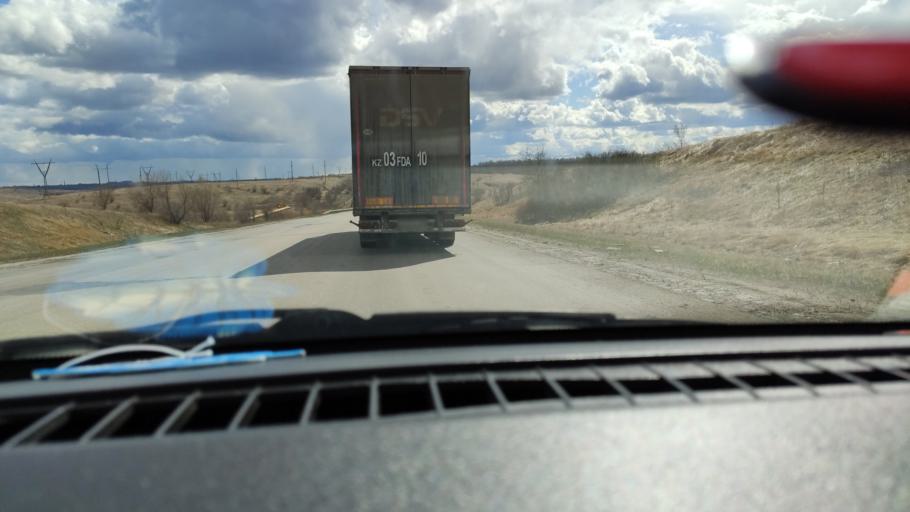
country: RU
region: Samara
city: Varlamovo
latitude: 53.0966
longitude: 48.3562
